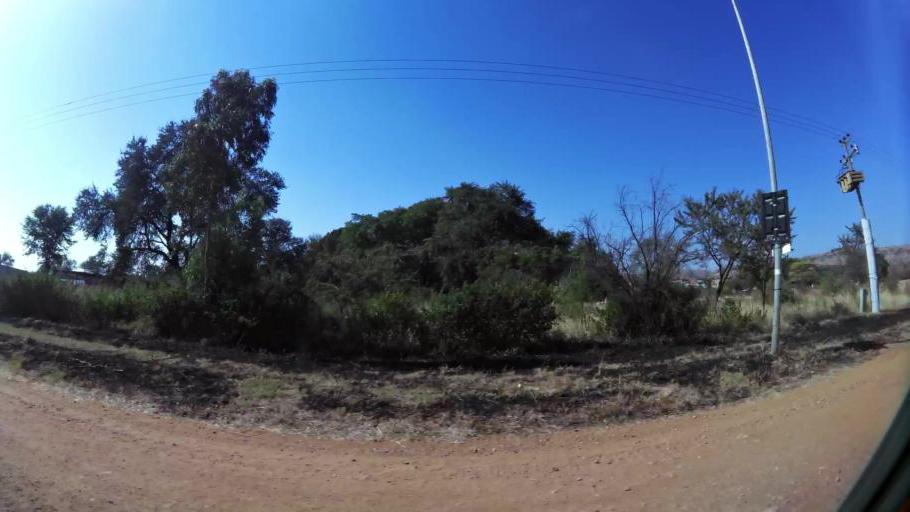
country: ZA
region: Gauteng
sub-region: City of Tshwane Metropolitan Municipality
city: Pretoria
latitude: -25.6697
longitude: 28.1010
